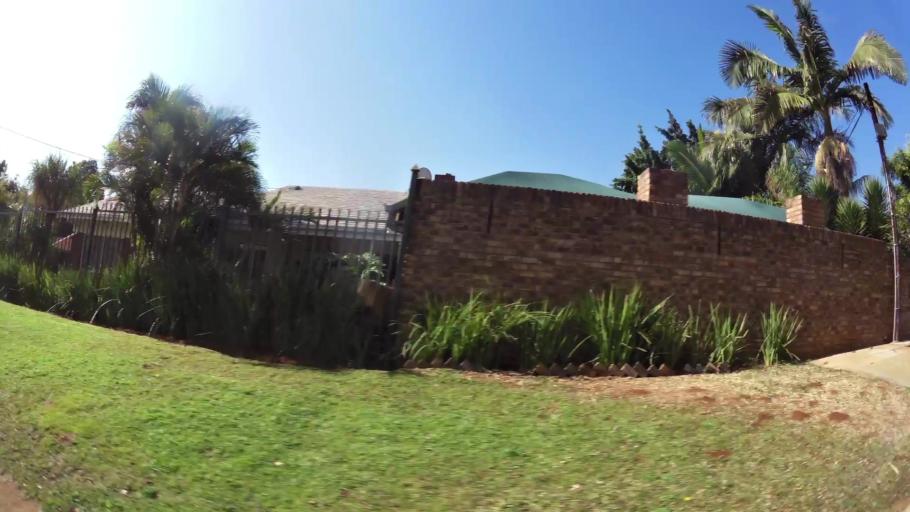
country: ZA
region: Gauteng
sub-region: City of Tshwane Metropolitan Municipality
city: Pretoria
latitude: -25.6872
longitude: 28.2219
